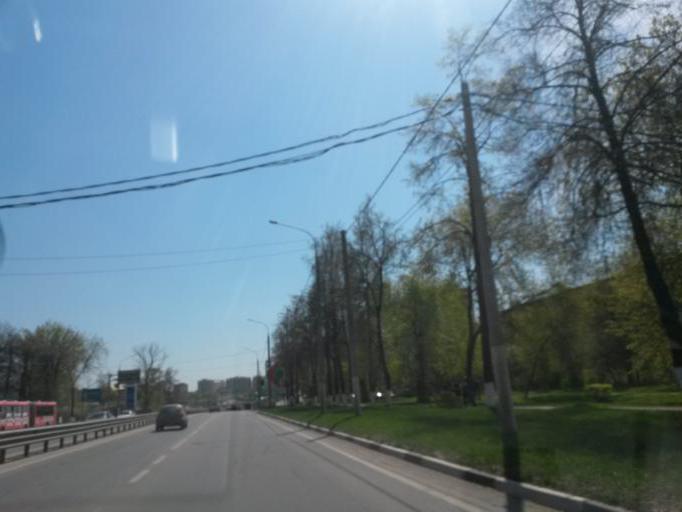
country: RU
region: Moskovskaya
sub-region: Podol'skiy Rayon
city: Podol'sk
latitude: 55.4138
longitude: 37.5492
